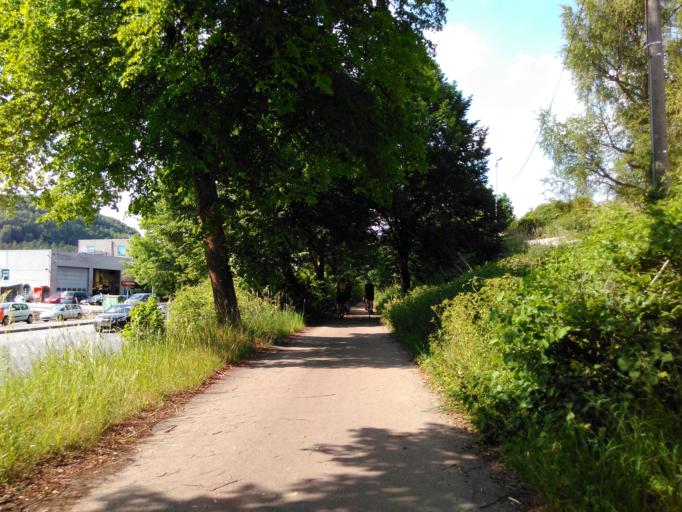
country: LU
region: Luxembourg
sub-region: Canton d'Esch-sur-Alzette
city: Rumelange
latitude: 49.4652
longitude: 6.0371
